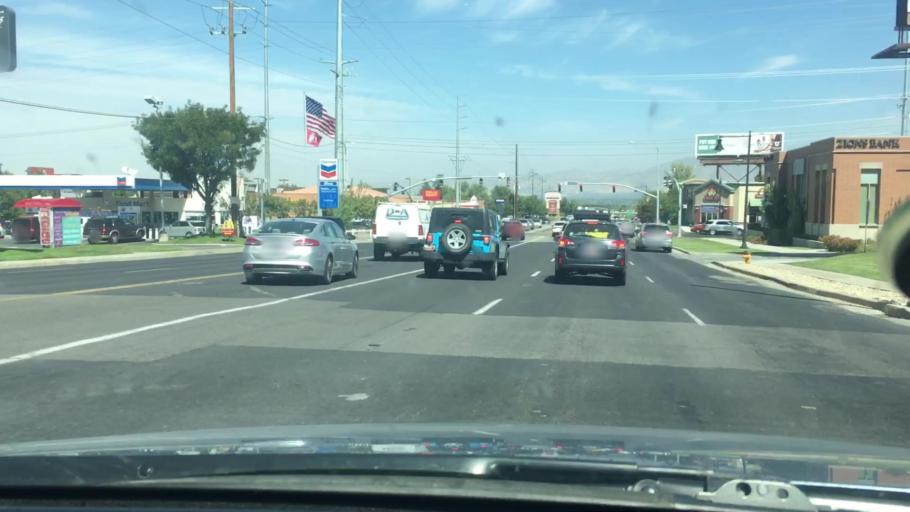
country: US
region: Utah
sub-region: Salt Lake County
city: Little Cottonwood Creek Valley
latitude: 40.6233
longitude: -111.8342
